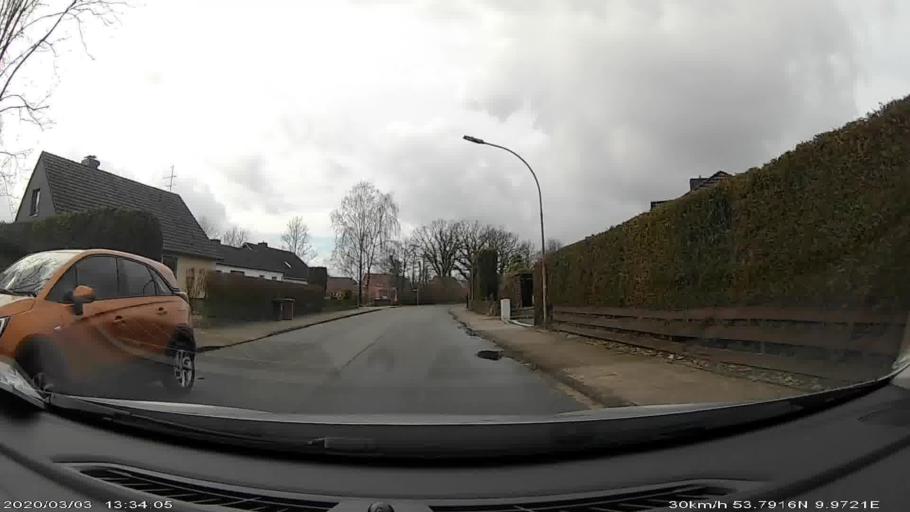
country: DE
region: Schleswig-Holstein
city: Henstedt-Ulzburg
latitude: 53.7917
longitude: 9.9711
